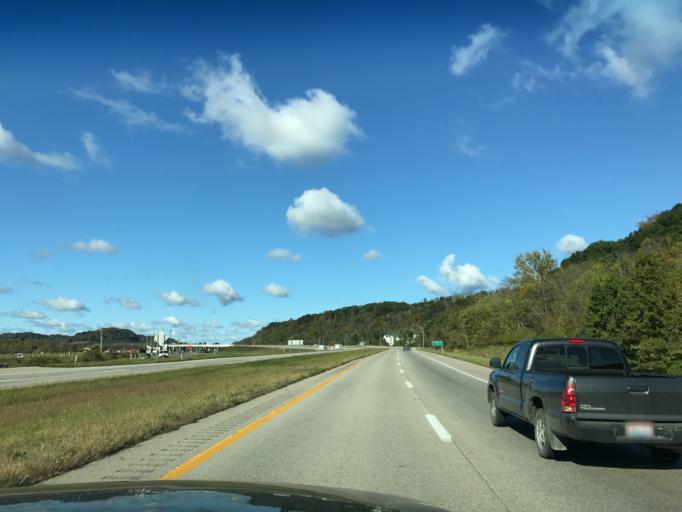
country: US
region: Ohio
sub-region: Athens County
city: Athens
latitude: 39.3345
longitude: -82.0261
